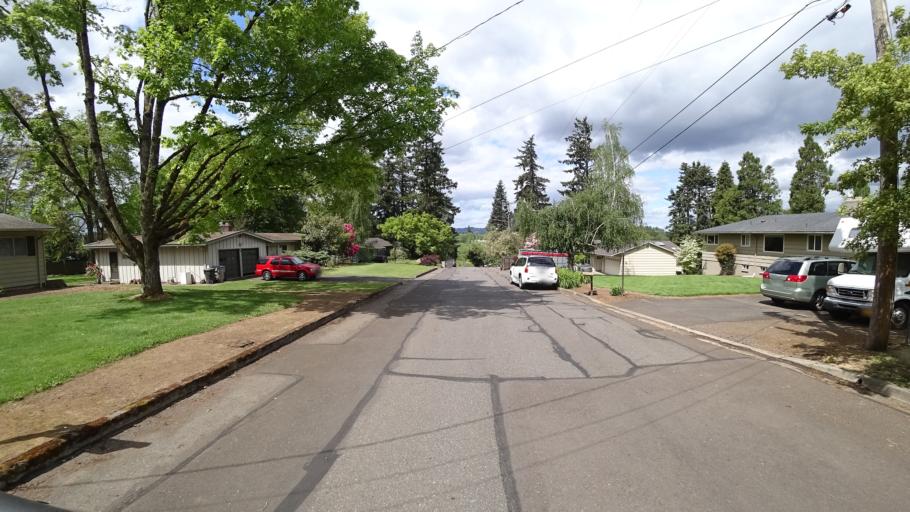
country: US
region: Oregon
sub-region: Washington County
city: Metzger
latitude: 45.4308
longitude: -122.7524
